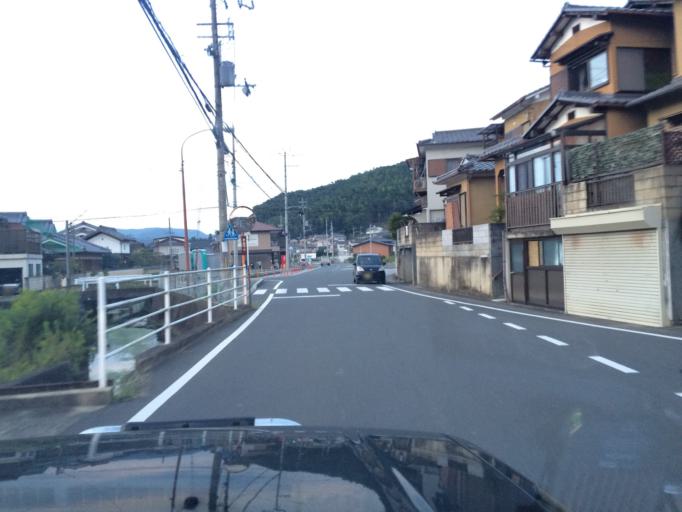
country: JP
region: Kyoto
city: Kameoka
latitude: 35.0981
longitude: 135.4746
